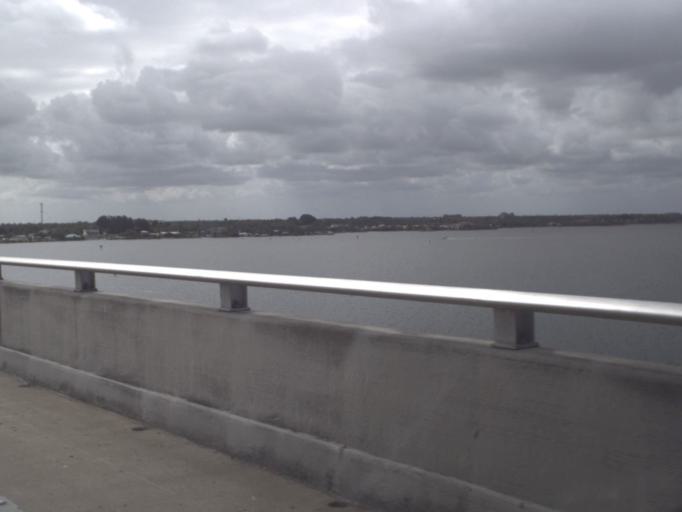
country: US
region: Florida
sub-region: Brevard County
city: South Patrick Shores
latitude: 28.2065
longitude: -80.6501
